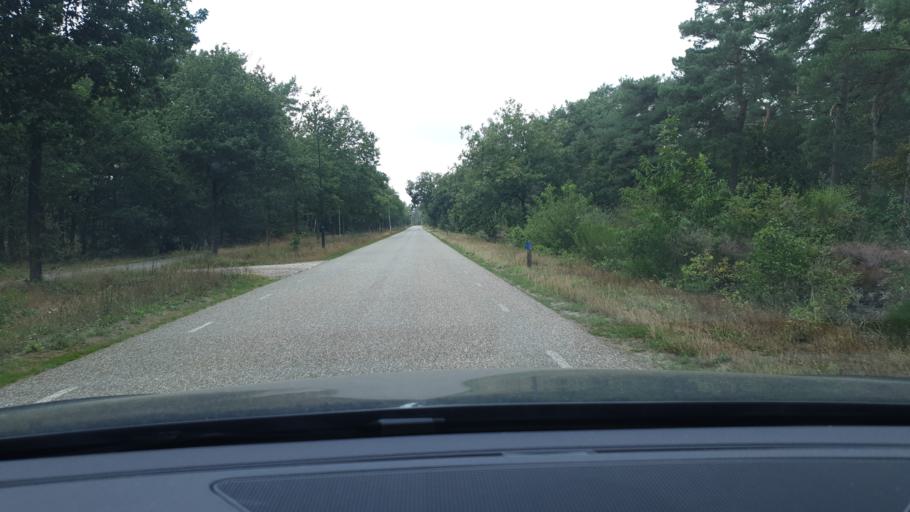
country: NL
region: North Brabant
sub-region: Gemeente Oirschot
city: Oostelbeers
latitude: 51.4565
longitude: 5.2809
